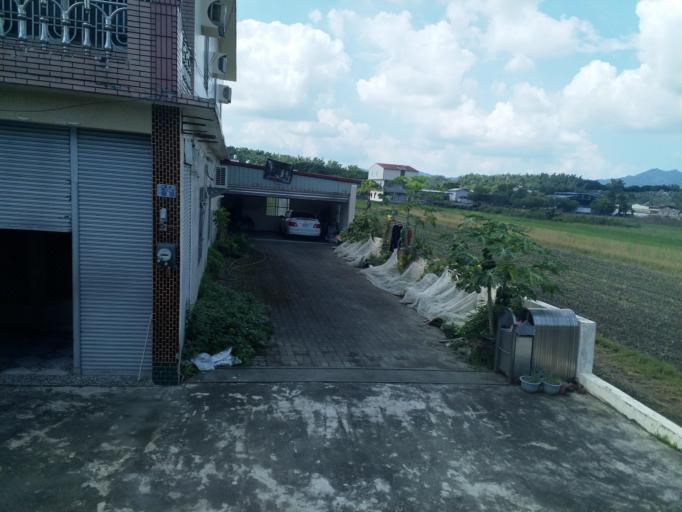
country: TW
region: Taiwan
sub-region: Pingtung
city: Pingtung
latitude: 22.8763
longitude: 120.5745
